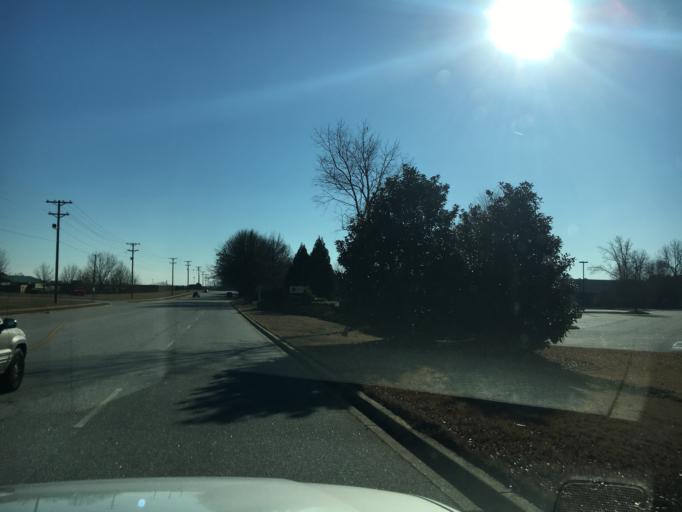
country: US
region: South Carolina
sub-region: Greenville County
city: Mauldin
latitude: 34.8076
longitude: -82.2759
